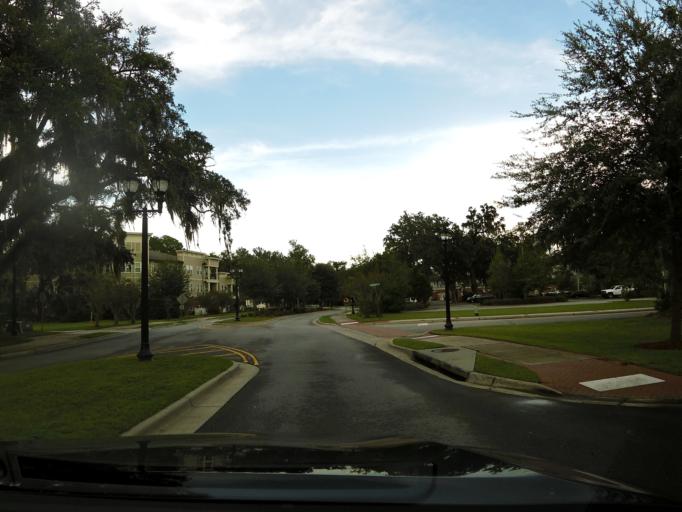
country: US
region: Georgia
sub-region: Liberty County
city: Hinesville
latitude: 31.8498
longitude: -81.5953
